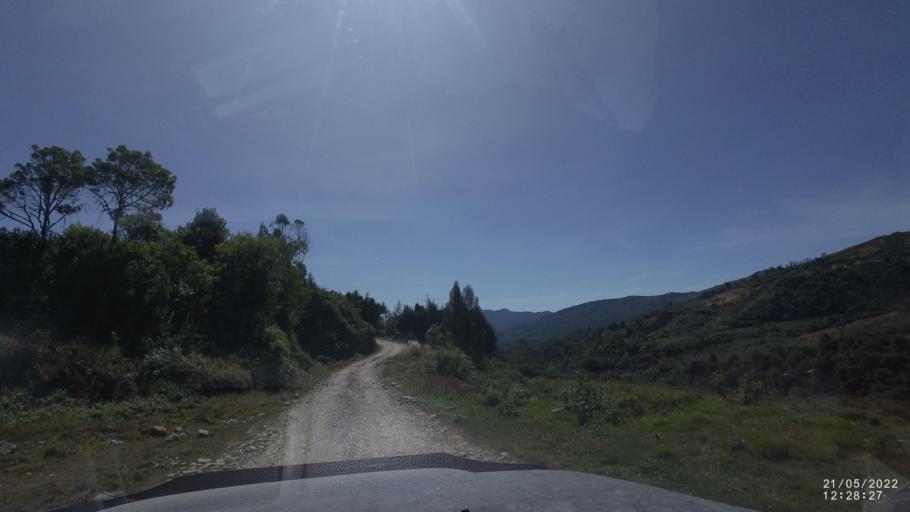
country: BO
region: Cochabamba
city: Colomi
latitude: -17.2182
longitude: -65.9119
